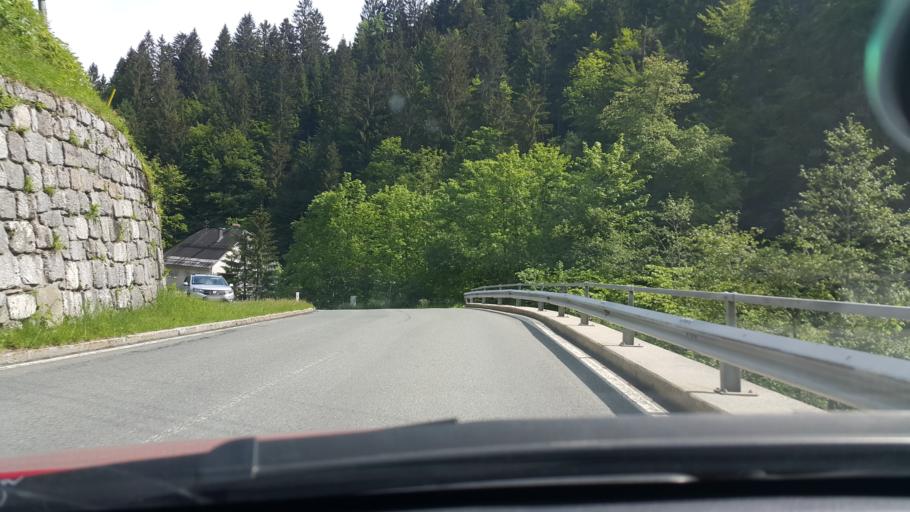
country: AT
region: Carinthia
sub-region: Politischer Bezirk Klagenfurt Land
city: Ferlach
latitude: 46.4643
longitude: 14.2576
